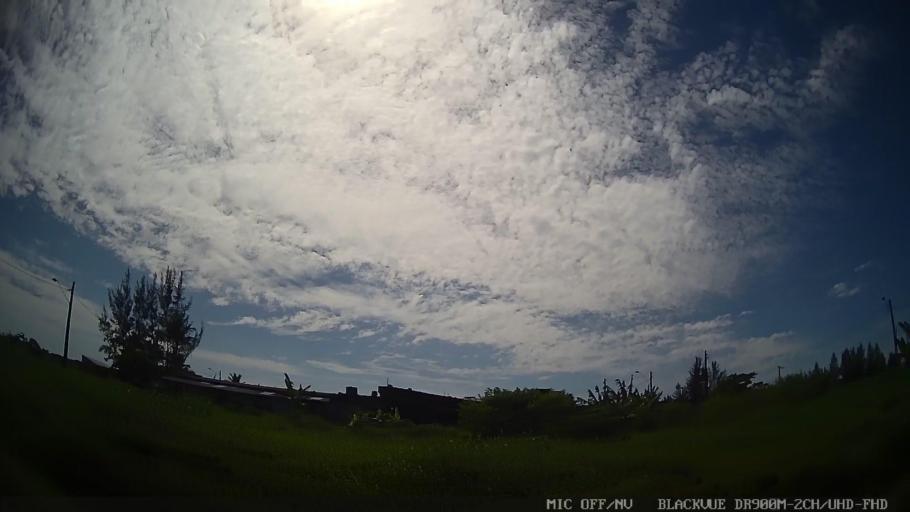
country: BR
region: Sao Paulo
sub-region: Iguape
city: Iguape
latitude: -24.7878
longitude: -47.6134
